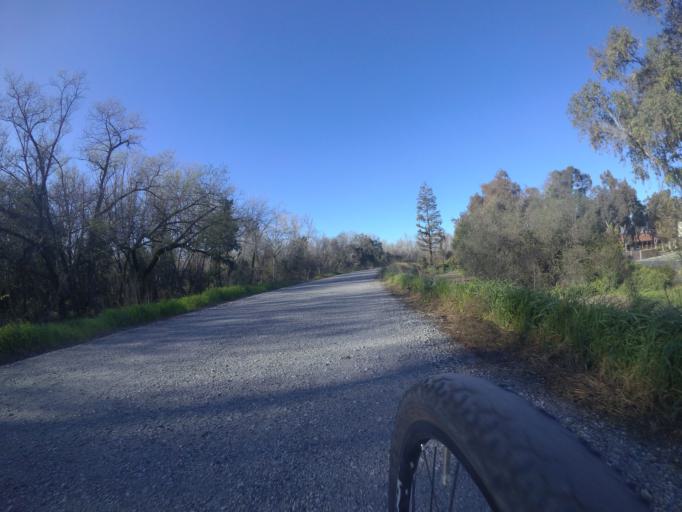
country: US
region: California
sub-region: Santa Clara County
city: Milpitas
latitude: 37.4076
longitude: -121.9228
